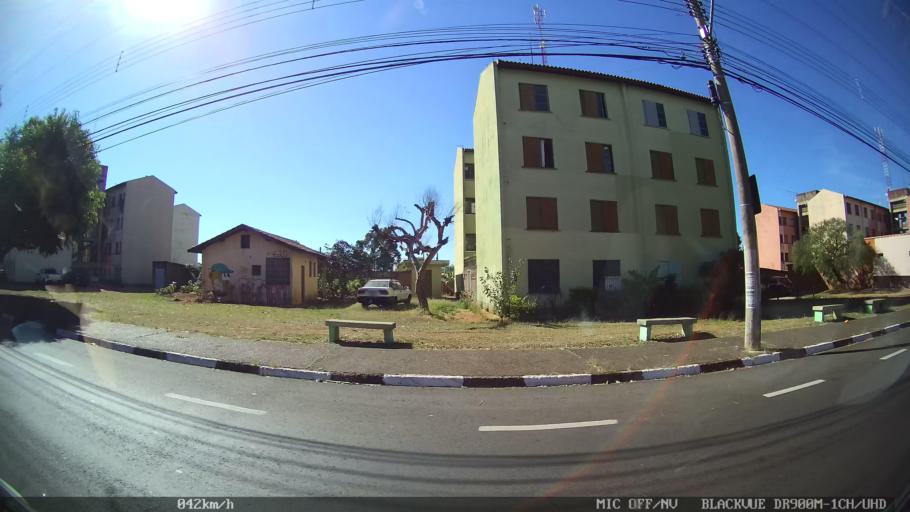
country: BR
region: Sao Paulo
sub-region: Franca
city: Franca
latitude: -20.5540
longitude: -47.3603
